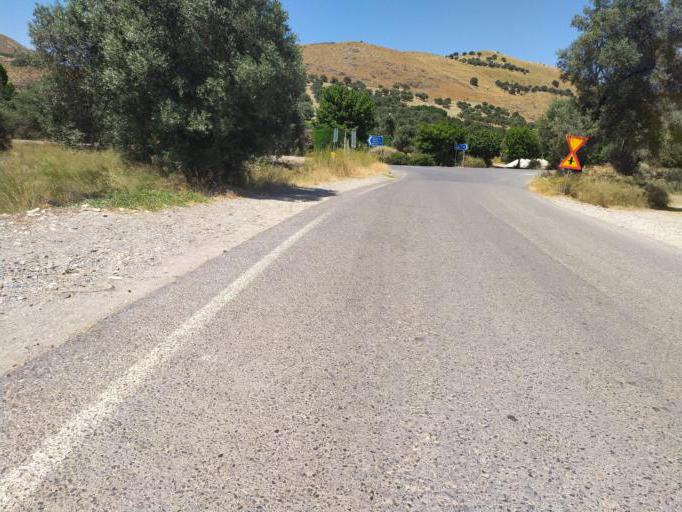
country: GR
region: Crete
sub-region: Nomos Irakleiou
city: Agioi Deka
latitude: 35.0610
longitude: 24.9478
